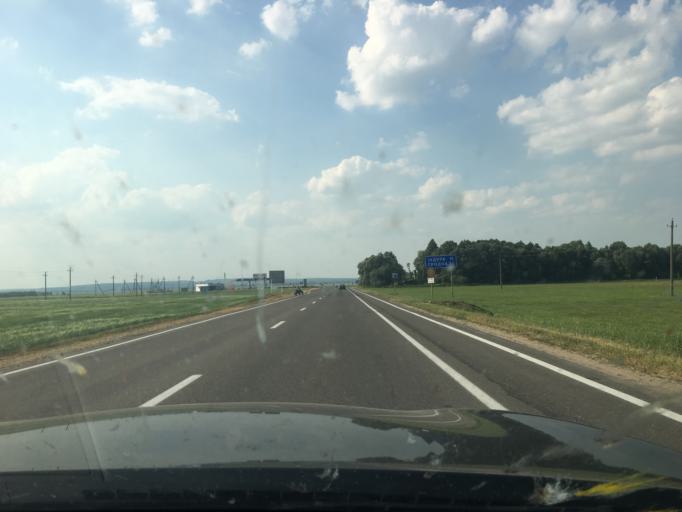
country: BY
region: Grodnenskaya
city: Indura
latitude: 53.3428
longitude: 23.9479
